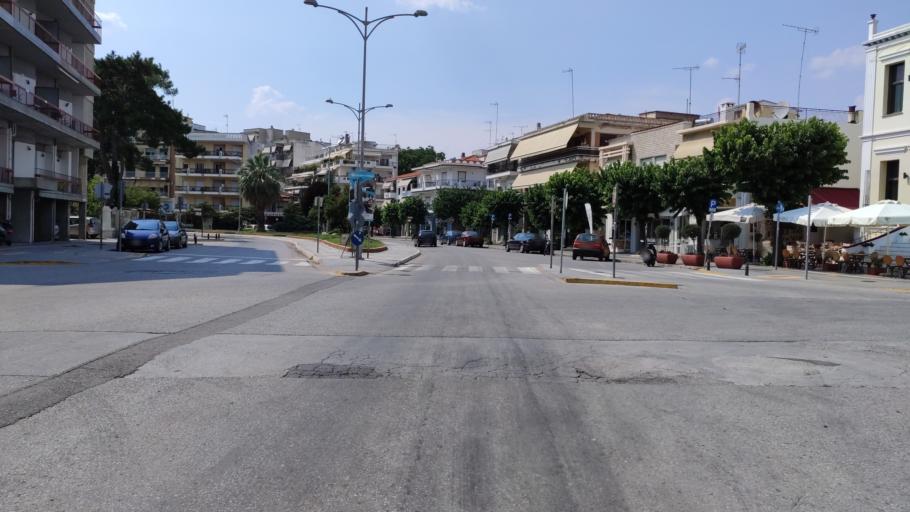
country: GR
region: East Macedonia and Thrace
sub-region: Nomos Rodopis
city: Komotini
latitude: 41.1193
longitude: 25.3997
